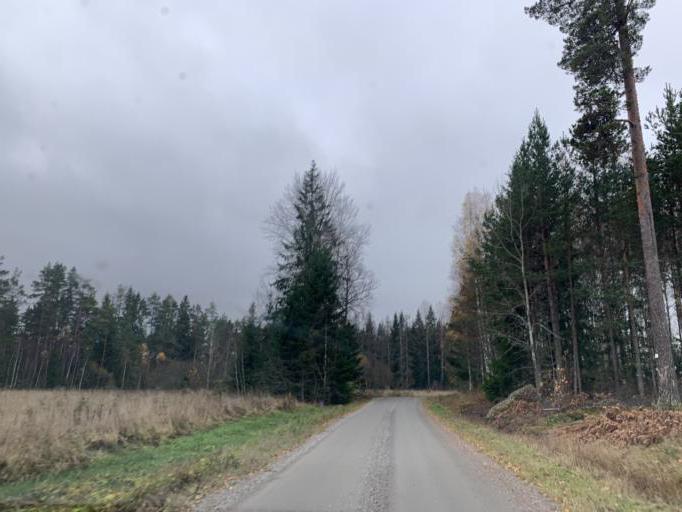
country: SE
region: Vaestmanland
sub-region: Surahammars Kommun
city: Ramnas
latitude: 59.7269
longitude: 16.0987
